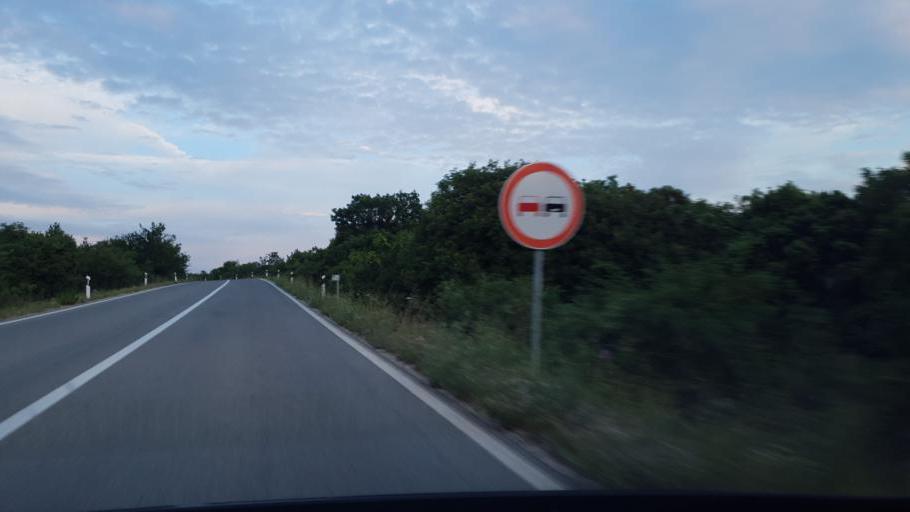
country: HR
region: Primorsko-Goranska
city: Punat
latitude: 45.0382
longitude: 14.6460
